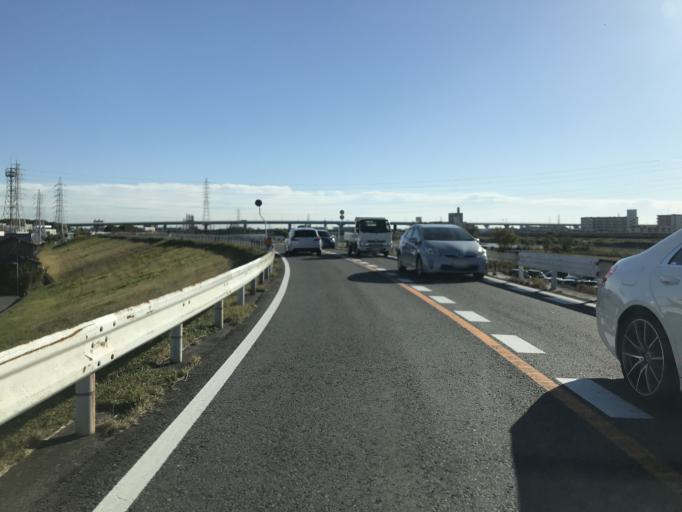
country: JP
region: Aichi
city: Kanie
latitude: 35.1643
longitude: 136.8356
